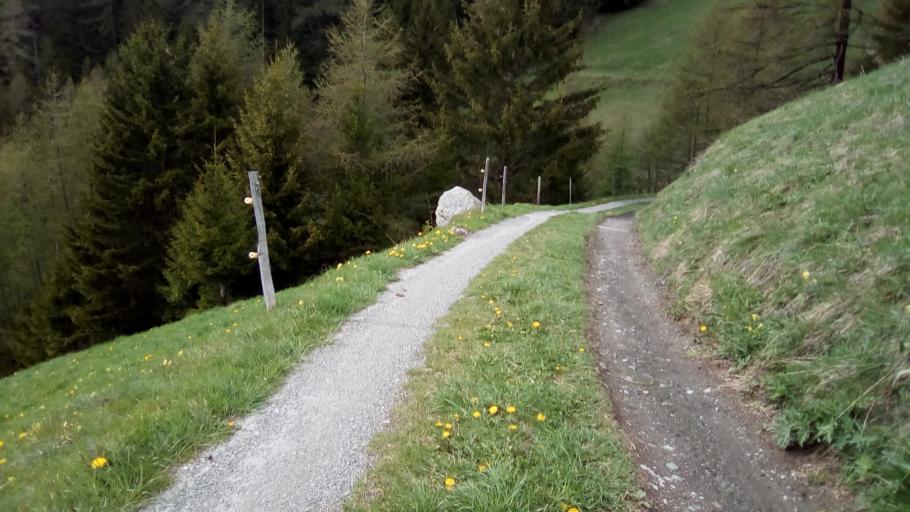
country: CH
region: Valais
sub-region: Entremont District
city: Orsieres
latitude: 46.0248
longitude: 7.1778
